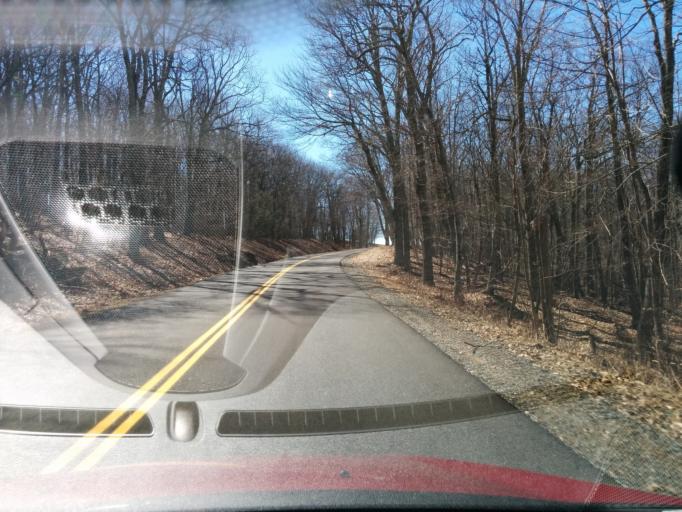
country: US
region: Virginia
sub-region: Augusta County
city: Stuarts Draft
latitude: 37.9044
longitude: -79.1032
